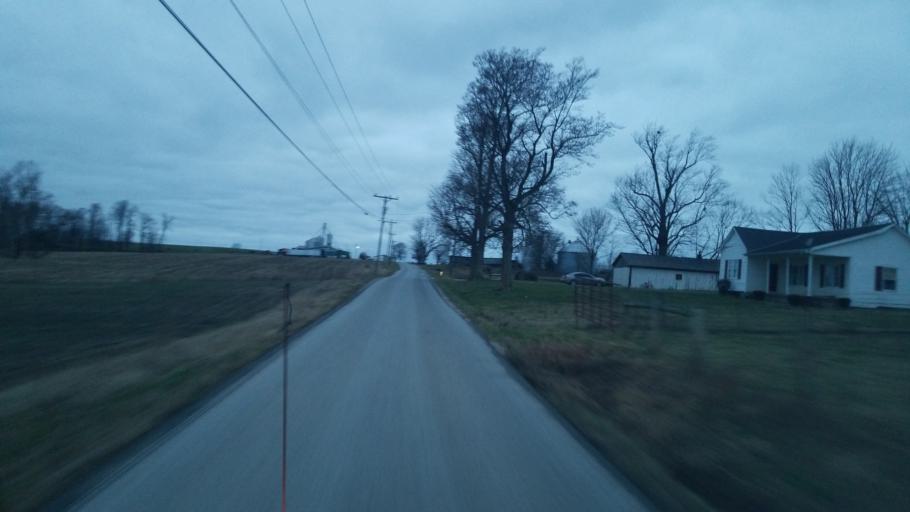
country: US
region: Kentucky
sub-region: Fleming County
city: Flemingsburg
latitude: 38.4864
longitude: -83.6514
